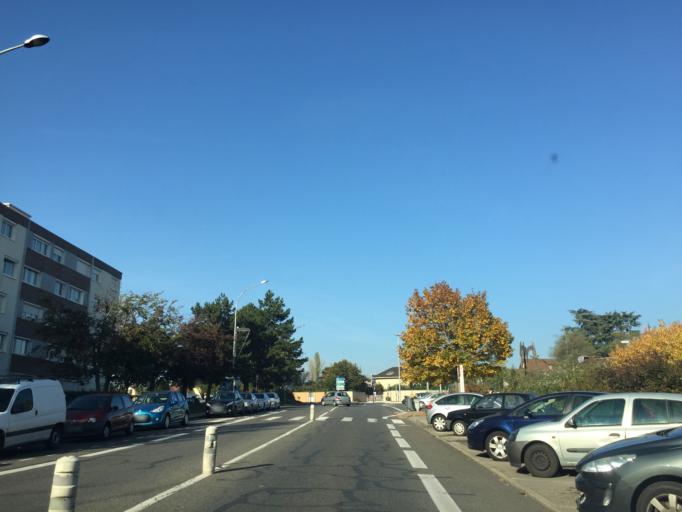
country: FR
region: Rhone-Alpes
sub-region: Departement du Rhone
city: Rillieux-la-Pape
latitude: 45.8223
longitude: 4.9073
